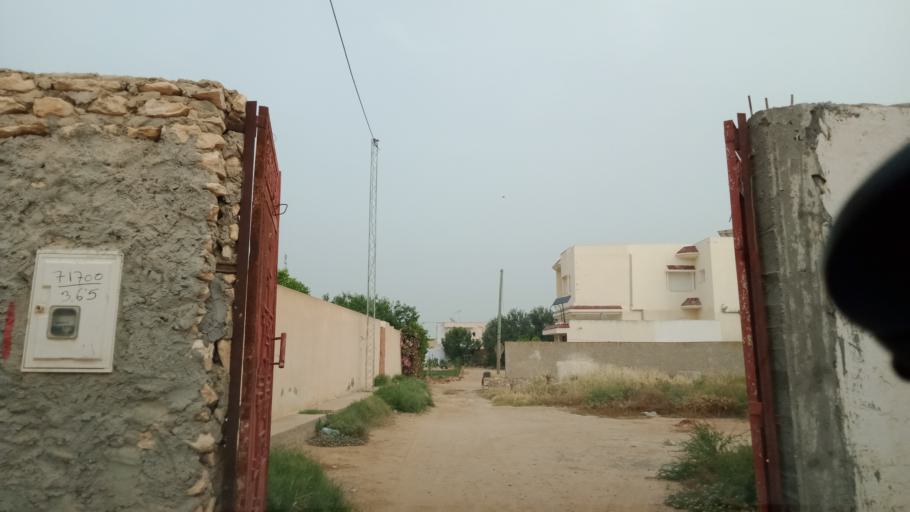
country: TN
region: Safaqis
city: Al Qarmadah
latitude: 34.7947
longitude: 10.7658
